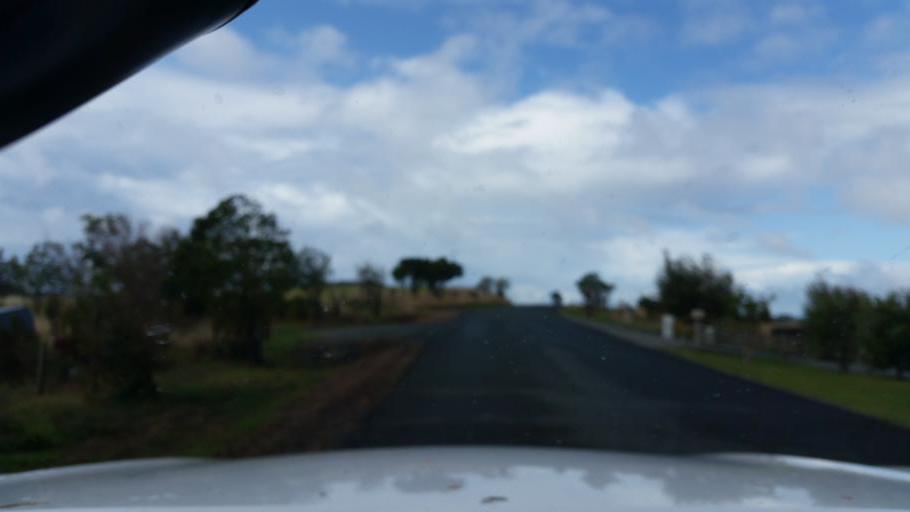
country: NZ
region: Auckland
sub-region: Auckland
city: Wellsford
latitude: -36.0847
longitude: 174.5629
